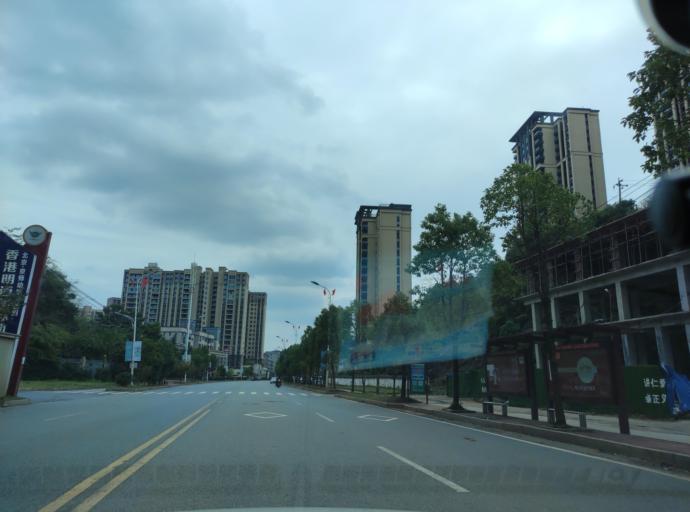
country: CN
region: Jiangxi Sheng
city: Pingxiang
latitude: 27.6785
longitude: 113.9080
